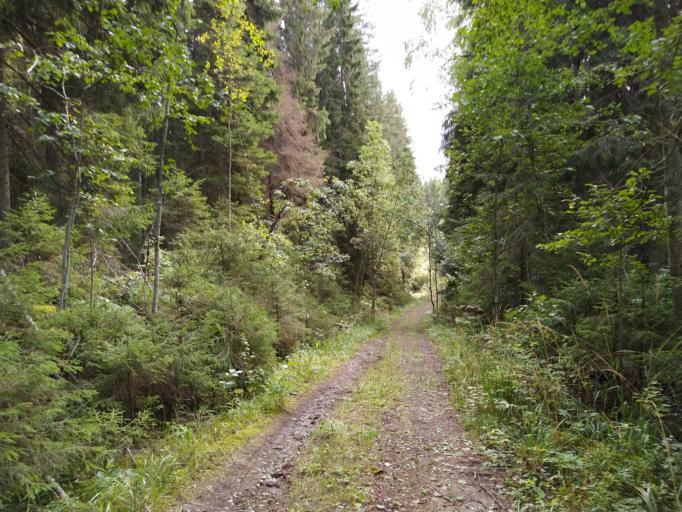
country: FI
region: Paijanne Tavastia
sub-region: Lahti
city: Auttoinen
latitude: 61.2294
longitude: 25.1675
